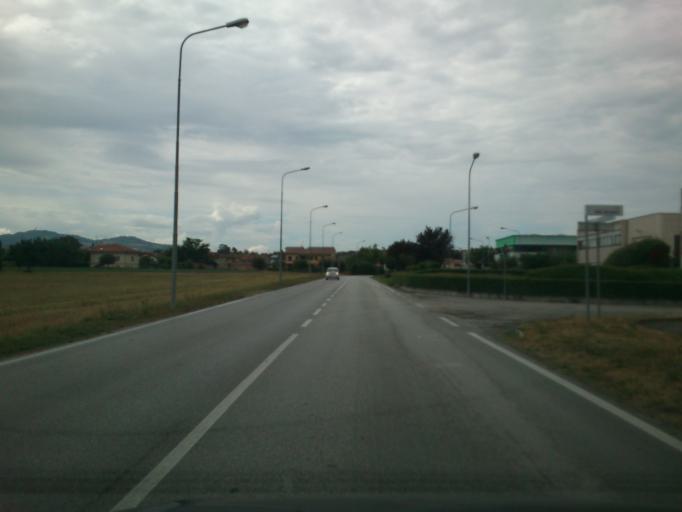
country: IT
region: The Marches
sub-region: Provincia di Pesaro e Urbino
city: Lucrezia
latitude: 43.7733
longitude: 12.9484
